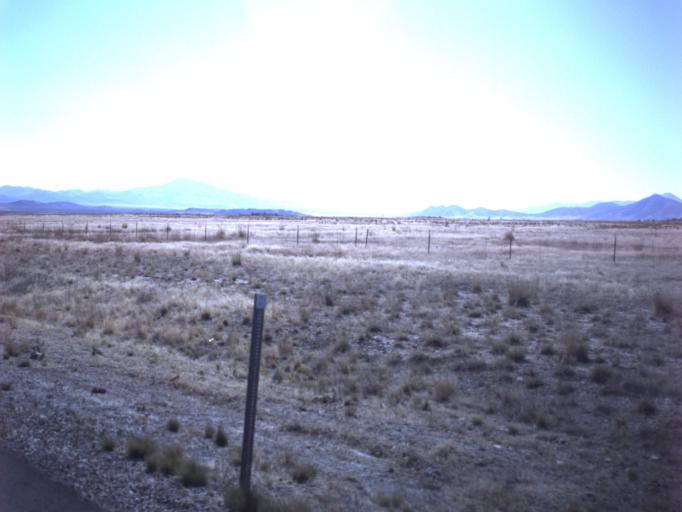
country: US
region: Utah
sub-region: Tooele County
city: Grantsville
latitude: 40.2519
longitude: -112.7349
